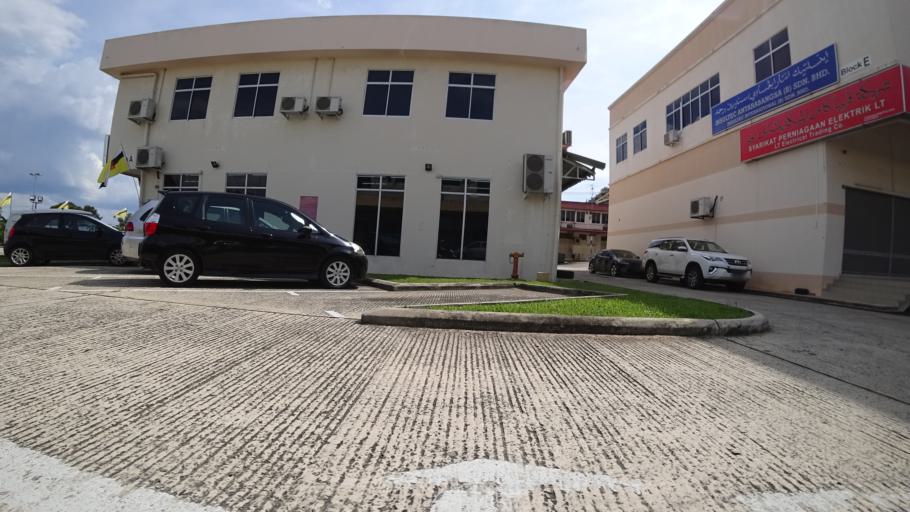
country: BN
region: Brunei and Muara
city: Bandar Seri Begawan
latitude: 4.8571
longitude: 114.8919
